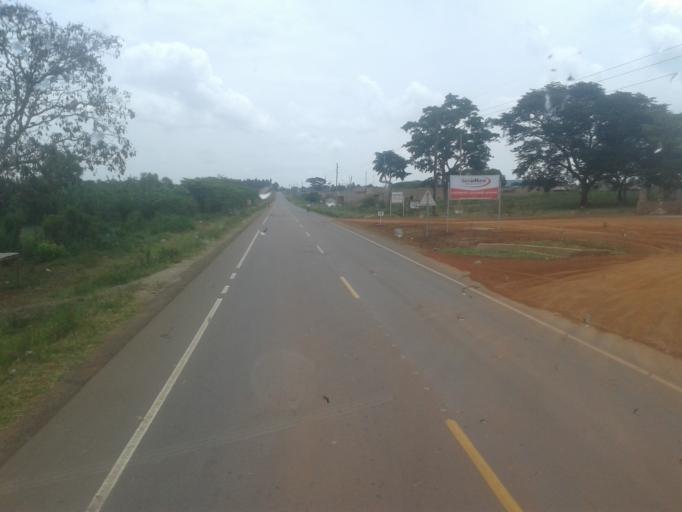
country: UG
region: Western Region
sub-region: Kiryandongo District
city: Kiryandongo
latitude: 1.7898
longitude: 32.0145
